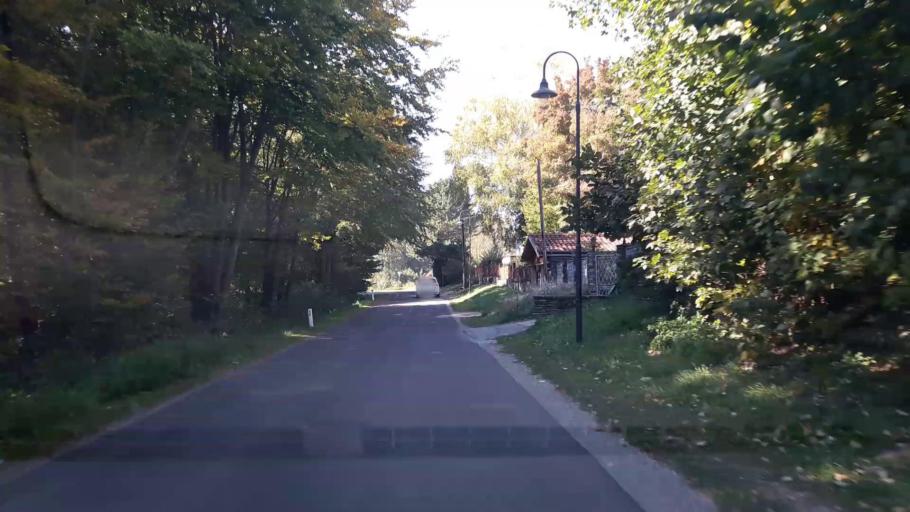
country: AT
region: Lower Austria
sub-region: Politischer Bezirk Korneuburg
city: Ernstbrunn
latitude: 48.5410
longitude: 16.3567
